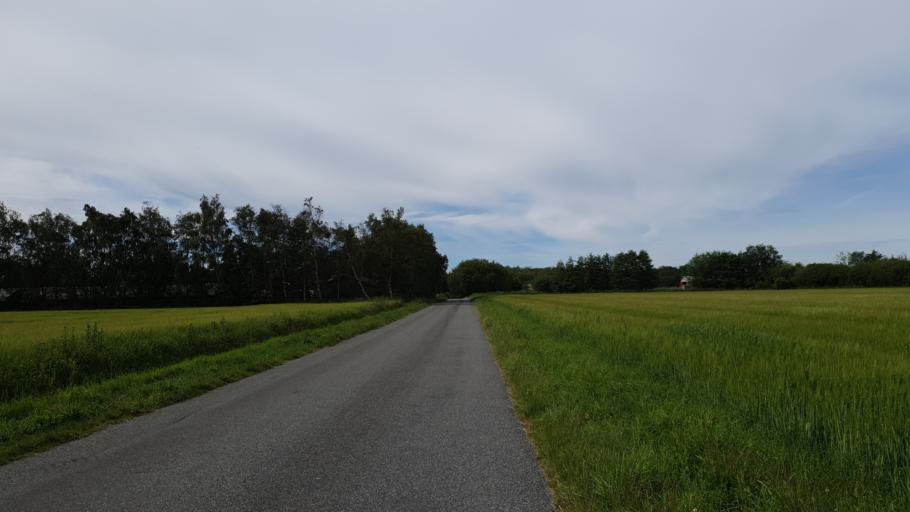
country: DK
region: North Denmark
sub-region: Laeso Kommune
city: Byrum
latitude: 57.2548
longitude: 10.9895
